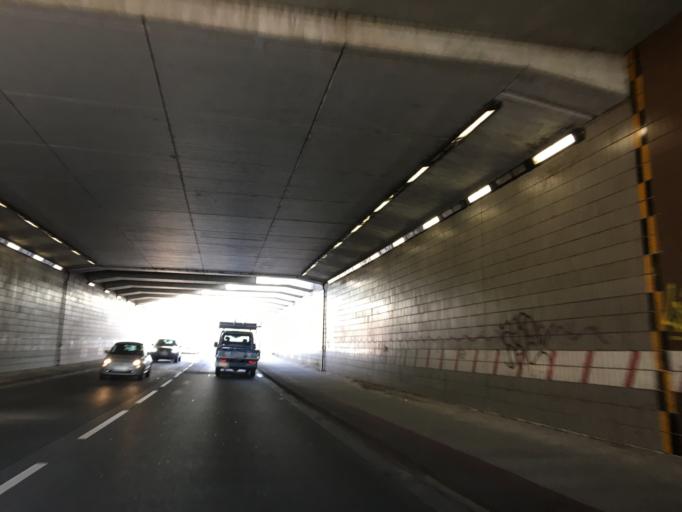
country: DE
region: Lower Saxony
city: Lueneburg
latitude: 53.2728
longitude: 10.4035
